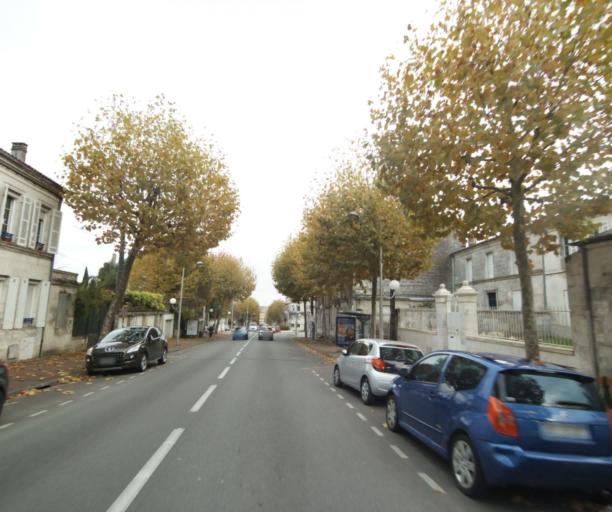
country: FR
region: Poitou-Charentes
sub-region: Departement de la Charente-Maritime
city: Saintes
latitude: 45.7475
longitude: -0.6386
